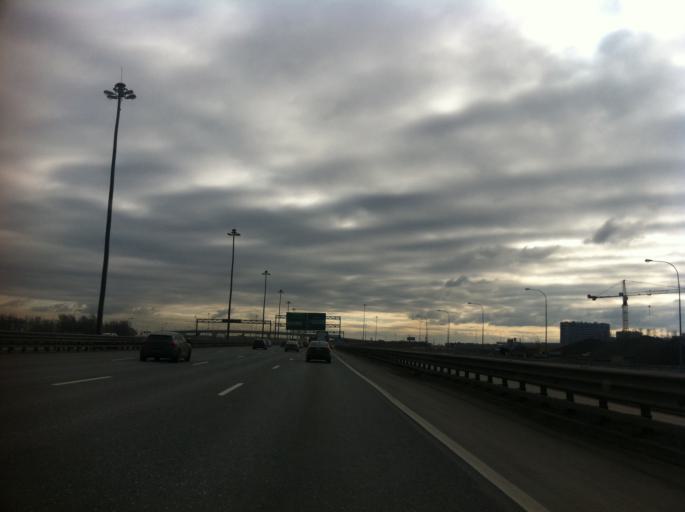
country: RU
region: St.-Petersburg
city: Dachnoye
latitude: 59.8172
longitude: 30.3095
